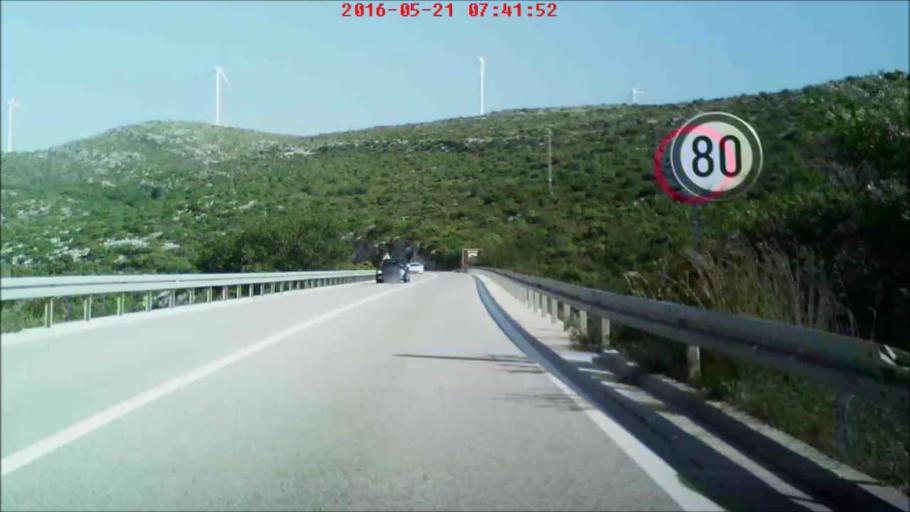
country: HR
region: Dubrovacko-Neretvanska
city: Podgora
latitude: 42.8068
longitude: 17.8102
